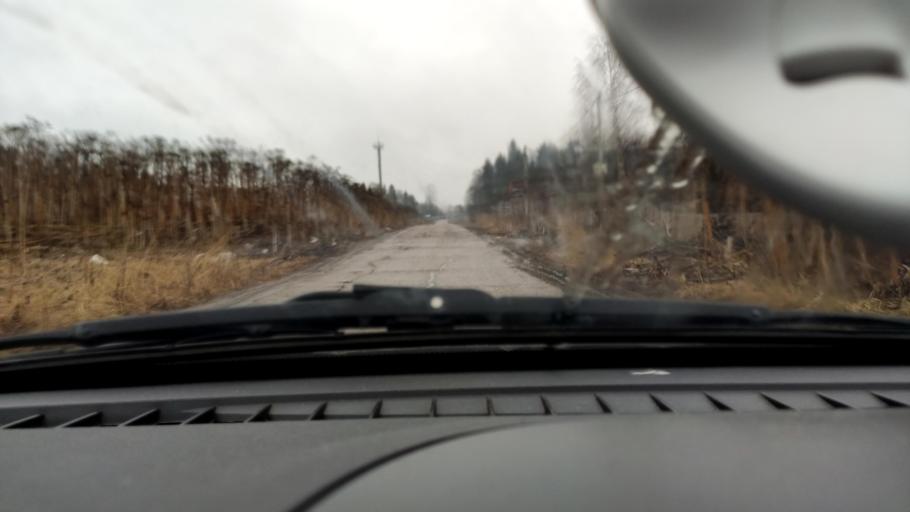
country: RU
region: Perm
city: Perm
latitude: 58.0341
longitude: 56.4114
